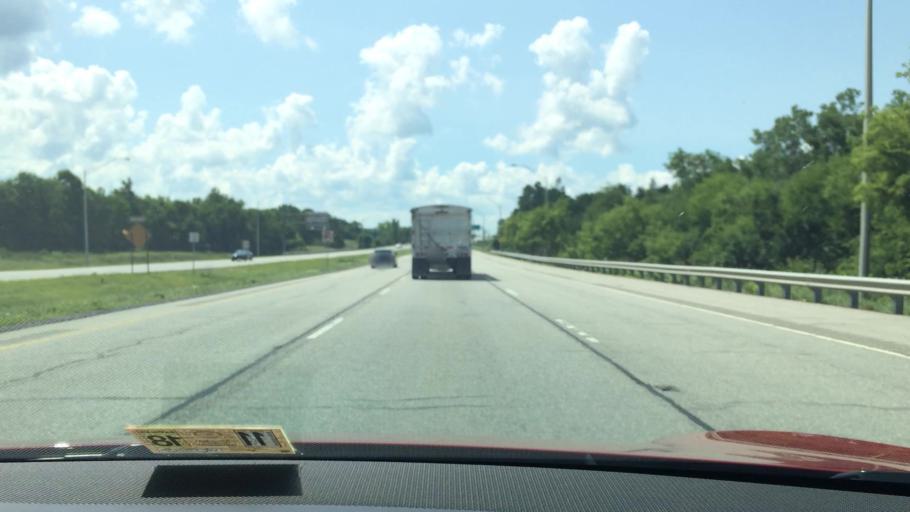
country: US
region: Indiana
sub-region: Saint Joseph County
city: South Bend
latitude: 41.7160
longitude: -86.3394
